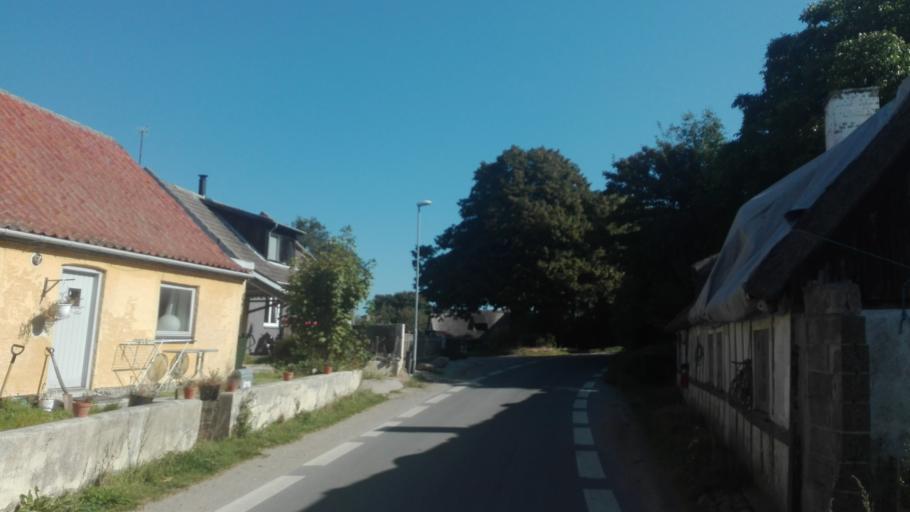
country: DK
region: Central Jutland
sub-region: Syddjurs Kommune
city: Ebeltoft
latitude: 56.2394
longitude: 10.7487
